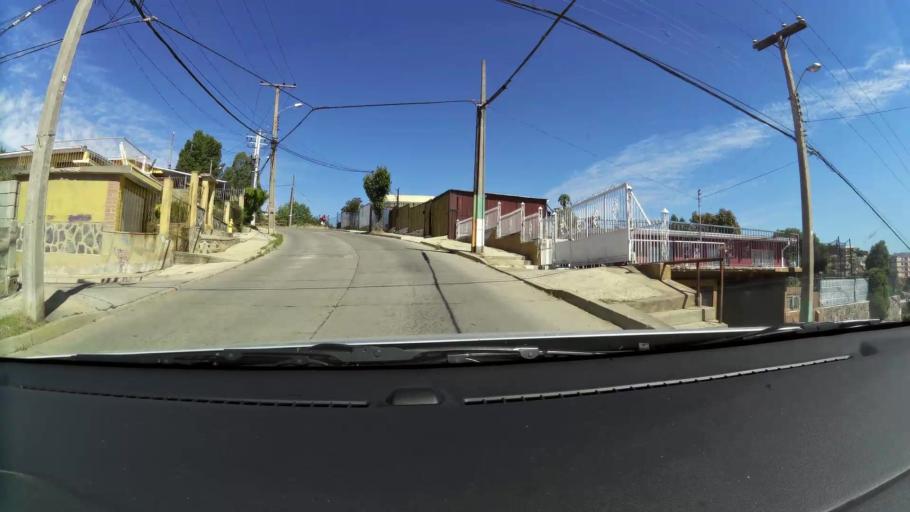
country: CL
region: Valparaiso
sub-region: Provincia de Valparaiso
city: Vina del Mar
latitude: -33.0424
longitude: -71.5717
